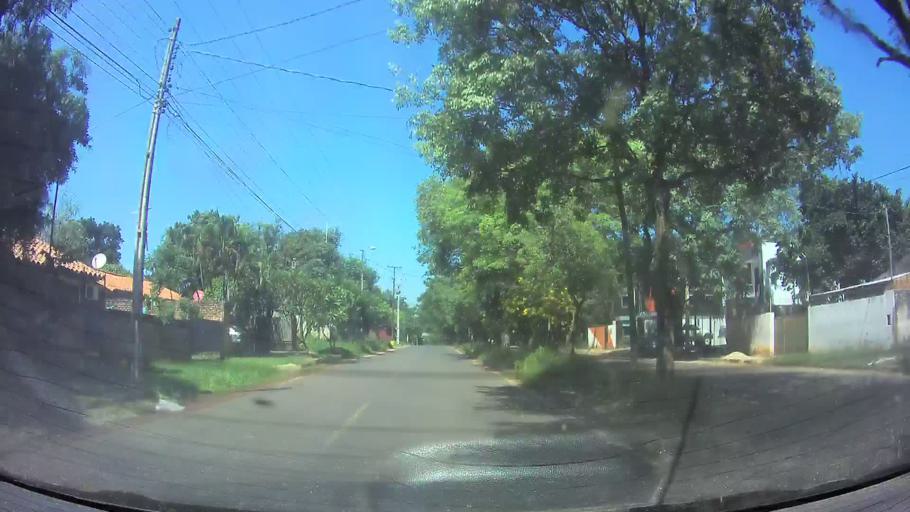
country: PY
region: Central
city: Fernando de la Mora
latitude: -25.2928
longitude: -57.5221
